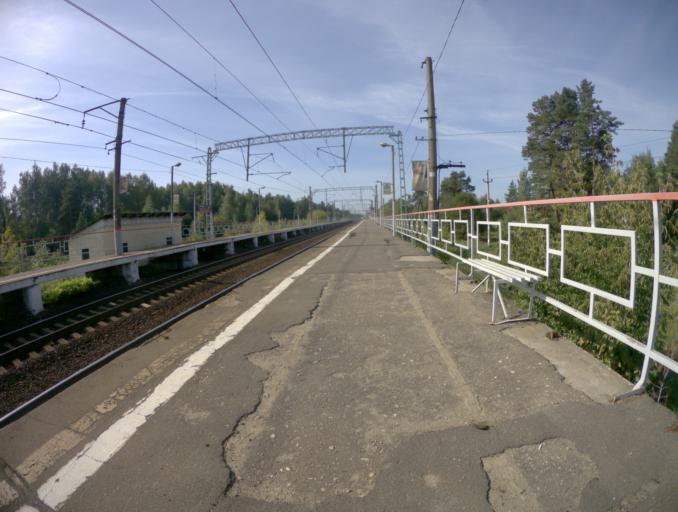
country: RU
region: Moskovskaya
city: Vereya
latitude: 55.8442
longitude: 39.0658
